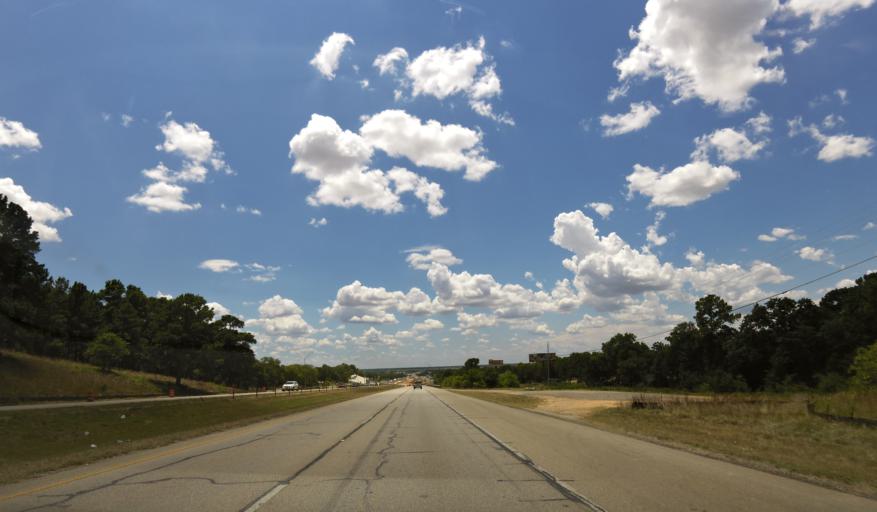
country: US
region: Texas
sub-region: Bastrop County
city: Bastrop
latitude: 30.1053
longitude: -97.2994
